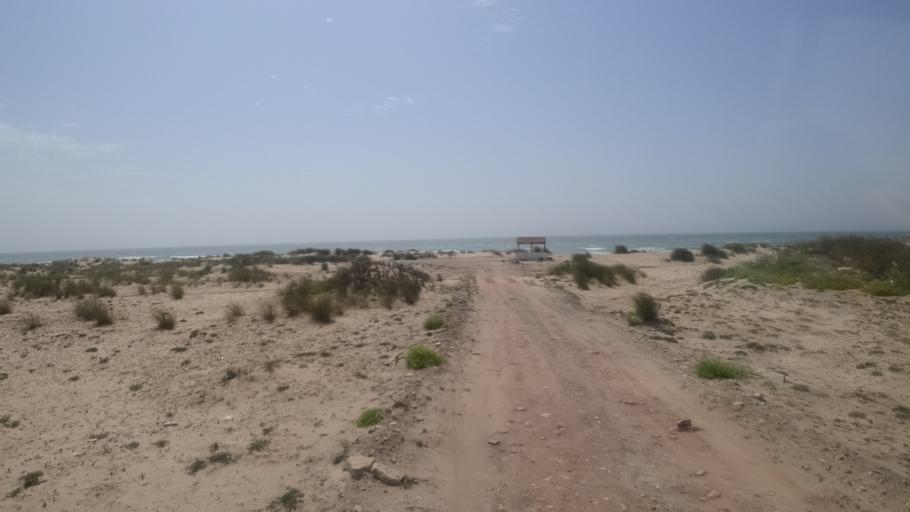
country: OM
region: Ash Sharqiyah
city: Sur
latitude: 22.1050
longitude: 59.7073
